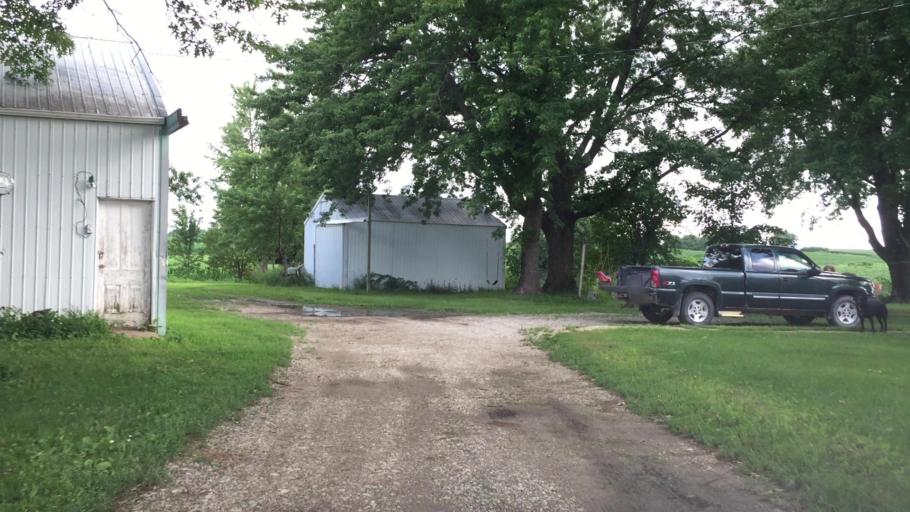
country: US
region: Iowa
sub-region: Jasper County
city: Monroe
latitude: 41.5805
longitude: -93.1115
